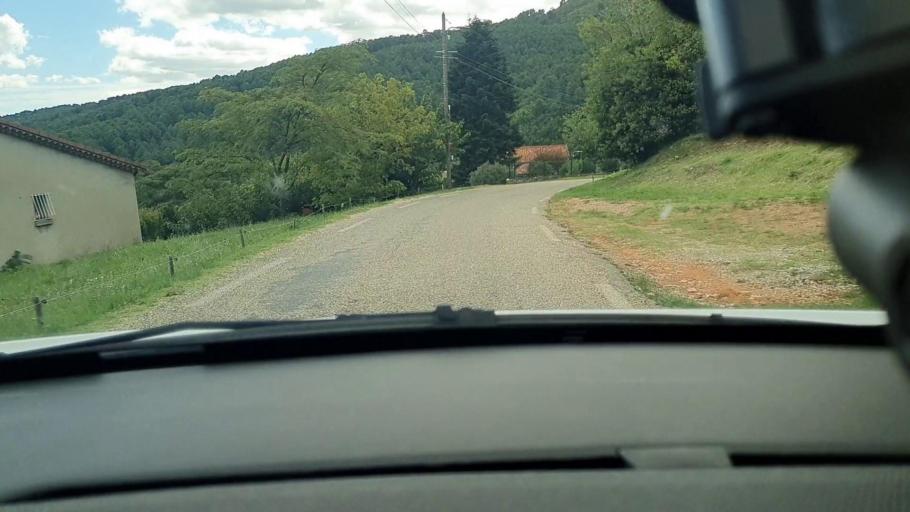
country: FR
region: Languedoc-Roussillon
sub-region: Departement du Gard
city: Branoux-les-Taillades
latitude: 44.2205
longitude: 3.9831
